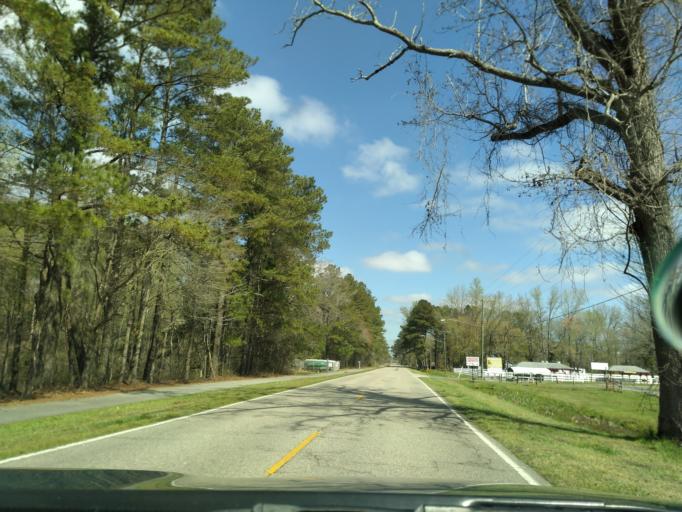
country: US
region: Virginia
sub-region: City of Portsmouth
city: Portsmouth Heights
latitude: 36.7126
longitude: -76.3528
